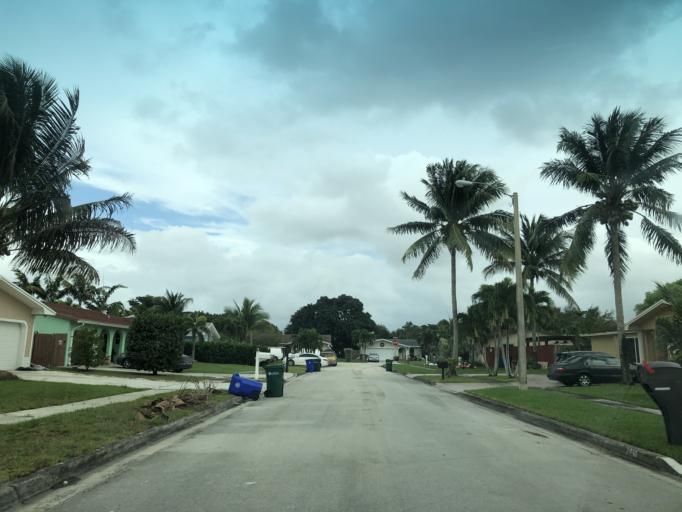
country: US
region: Florida
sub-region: Broward County
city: North Lauderdale
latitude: 26.2402
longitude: -80.2321
